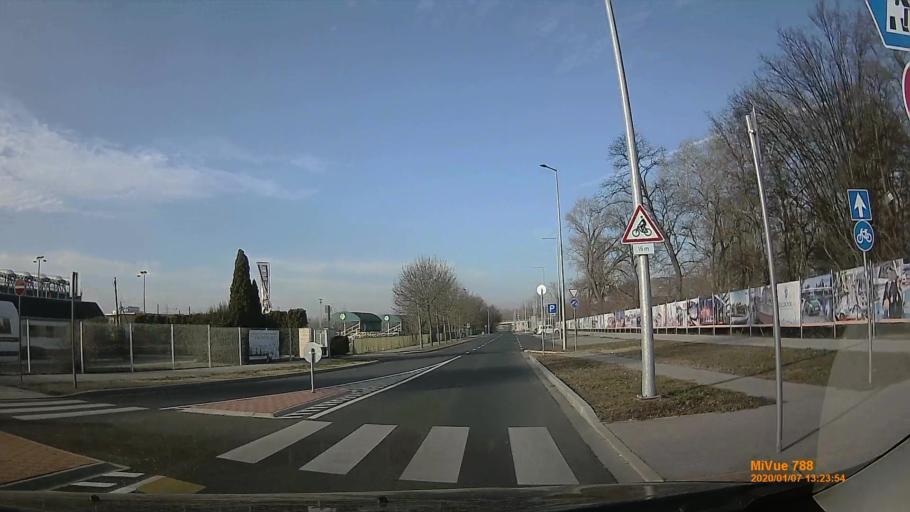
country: HU
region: Gyor-Moson-Sopron
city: Gyor
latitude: 47.6959
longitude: 17.6684
